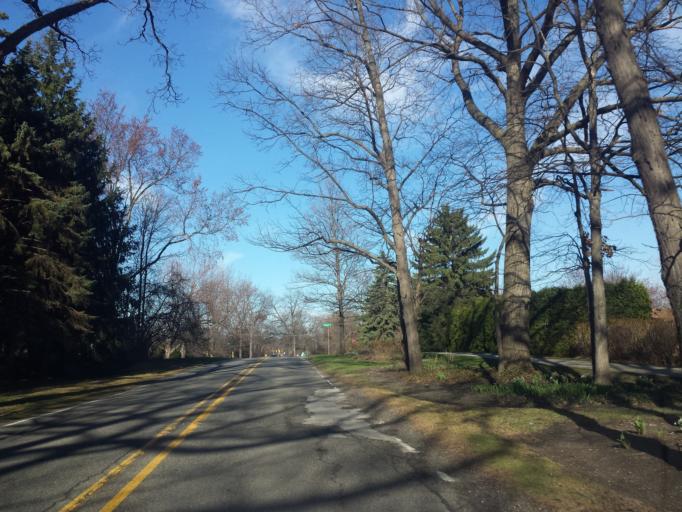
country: US
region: Michigan
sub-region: Oakland County
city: Bloomfield Hills
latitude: 42.5960
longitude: -83.2778
